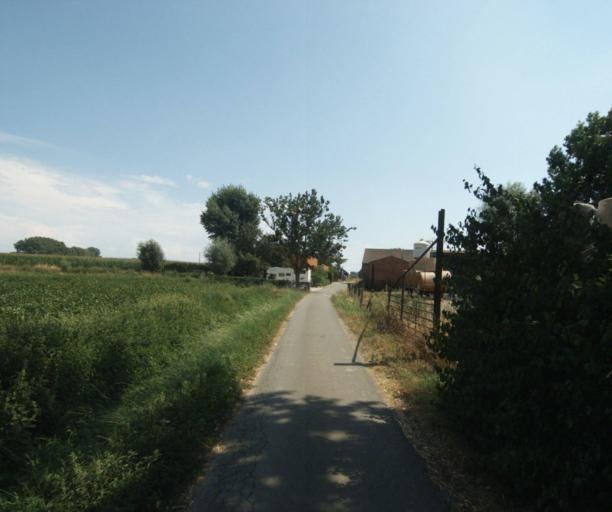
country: FR
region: Nord-Pas-de-Calais
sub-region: Departement du Nord
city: Quesnoy-sur-Deule
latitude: 50.7348
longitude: 3.0008
